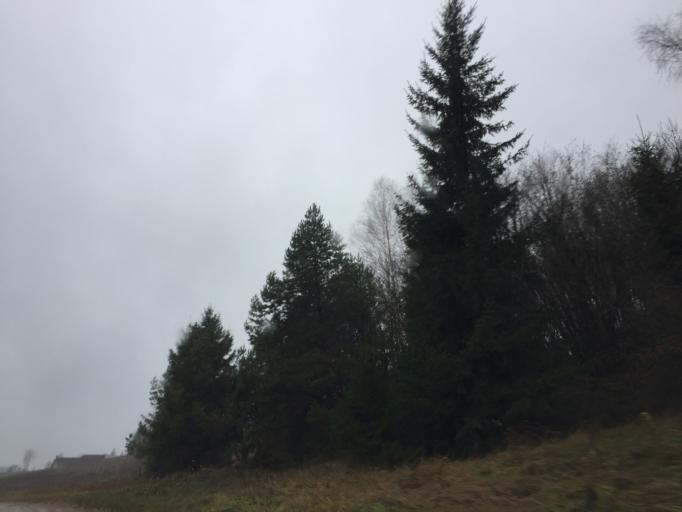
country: LV
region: Salas
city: Sala
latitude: 56.5012
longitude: 25.6902
